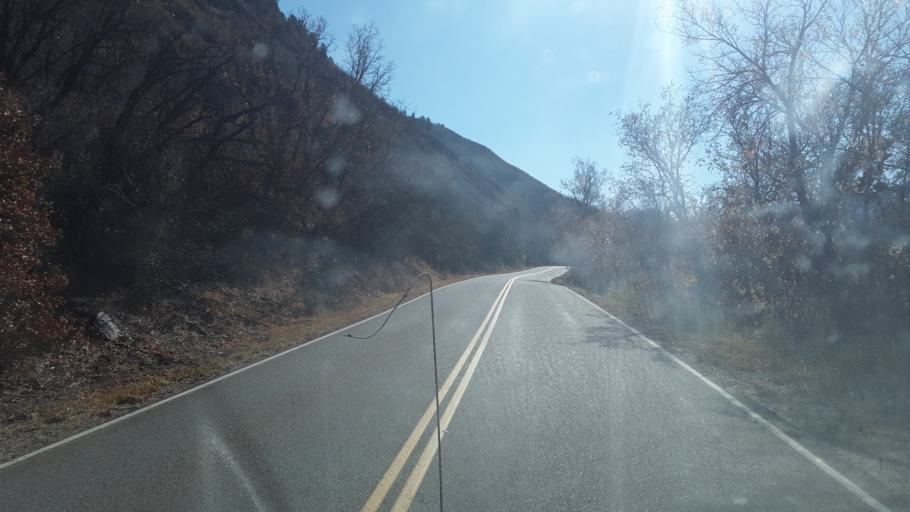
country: US
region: Colorado
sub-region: La Plata County
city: Durango
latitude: 37.3895
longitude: -107.8272
